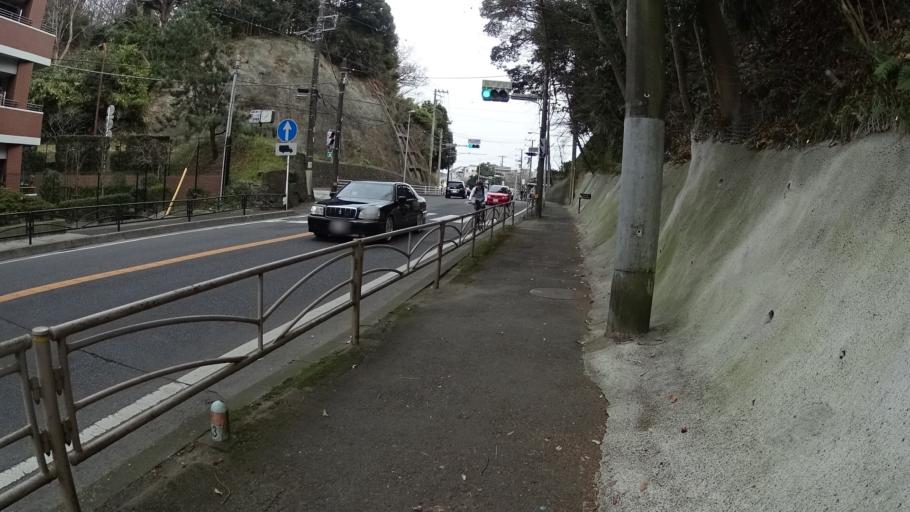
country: JP
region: Kanagawa
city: Oiso
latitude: 35.3039
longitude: 139.2902
